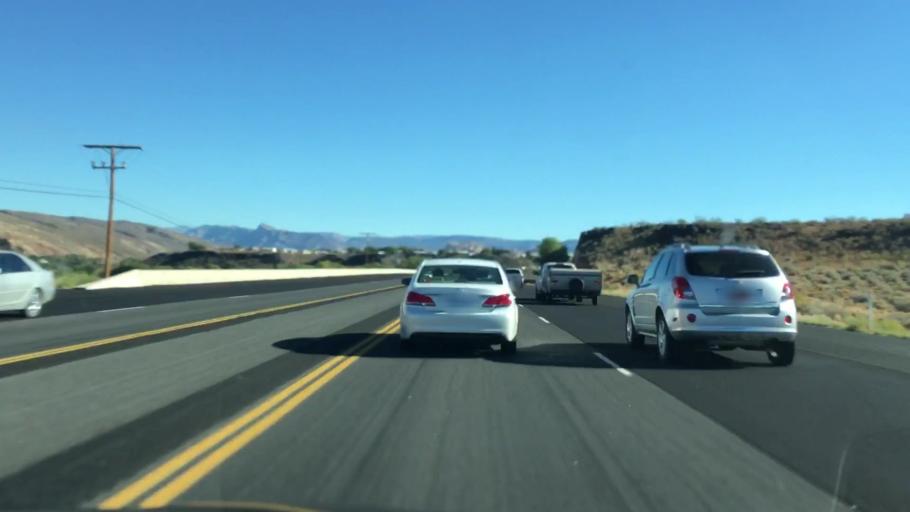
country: US
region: Utah
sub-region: Washington County
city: Hurricane
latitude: 37.1629
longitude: -113.3878
